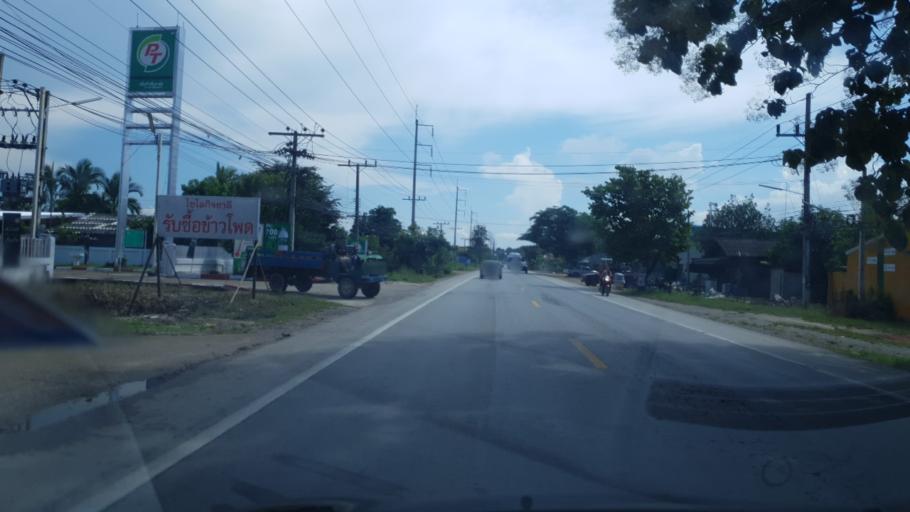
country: TH
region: Chiang Rai
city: Wiang Pa Pao
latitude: 19.3797
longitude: 99.5024
